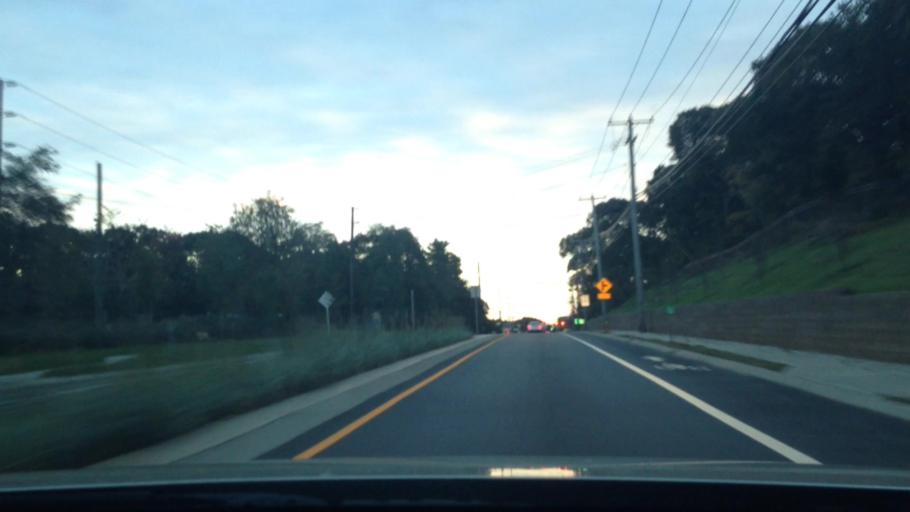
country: US
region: New York
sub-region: Suffolk County
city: Coram
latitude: 40.8510
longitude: -72.9977
